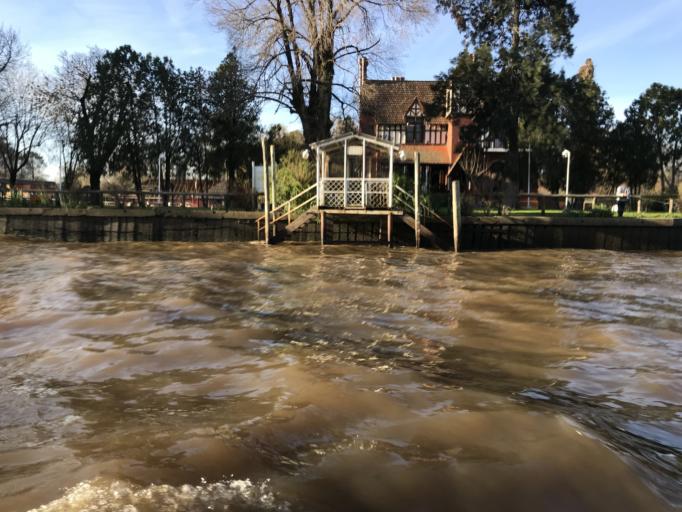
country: AR
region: Buenos Aires
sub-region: Partido de Tigre
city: Tigre
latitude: -34.4092
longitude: -58.5892
